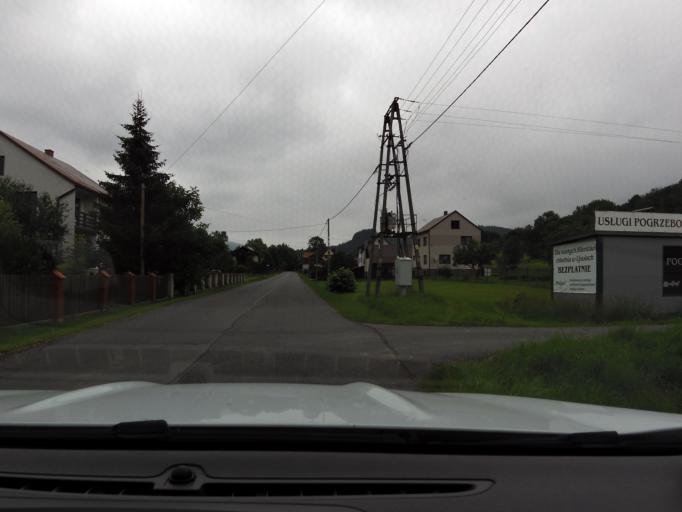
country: PL
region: Silesian Voivodeship
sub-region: Powiat zywiecki
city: Ujsoly
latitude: 49.4792
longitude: 19.1466
